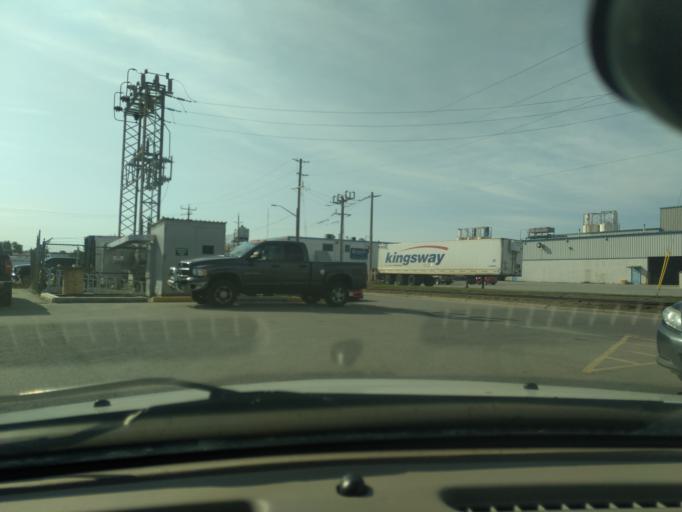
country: CA
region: Ontario
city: Barrie
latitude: 44.3763
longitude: -79.7033
